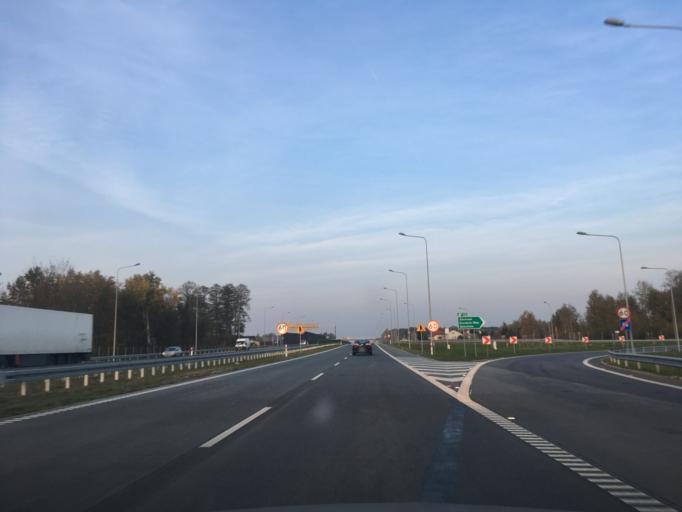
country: PL
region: Lodz Voivodeship
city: Zabia Wola
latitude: 52.0516
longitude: 20.7188
